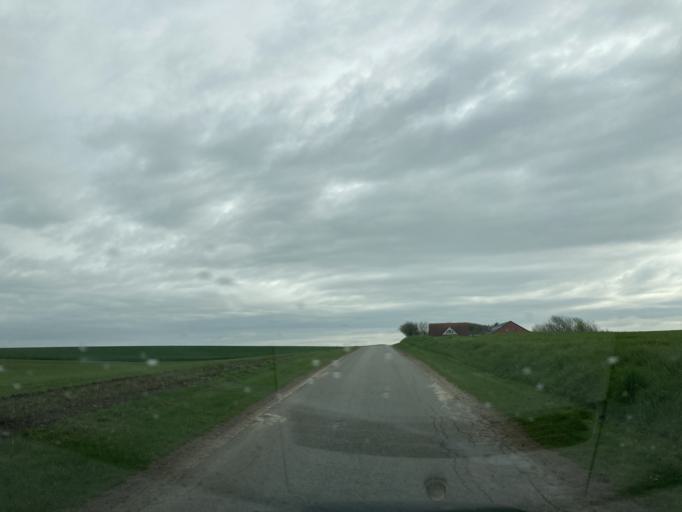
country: DK
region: North Denmark
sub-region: Thisted Kommune
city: Hanstholm
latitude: 57.0180
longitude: 8.5914
